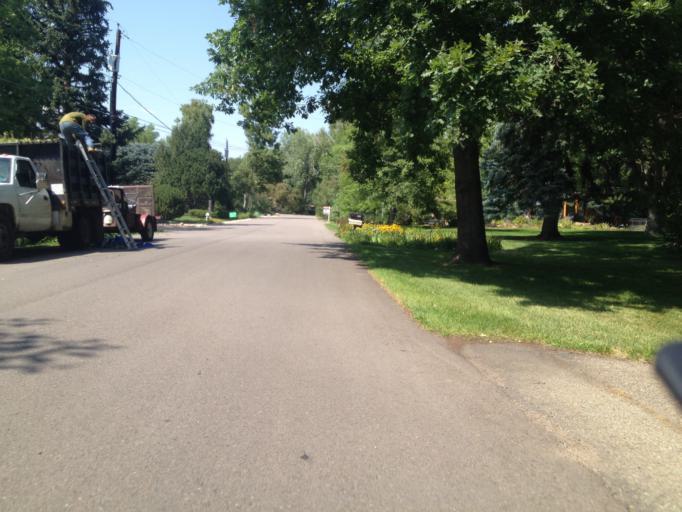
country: US
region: Colorado
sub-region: Boulder County
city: Boulder
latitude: 40.0098
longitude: -105.2160
